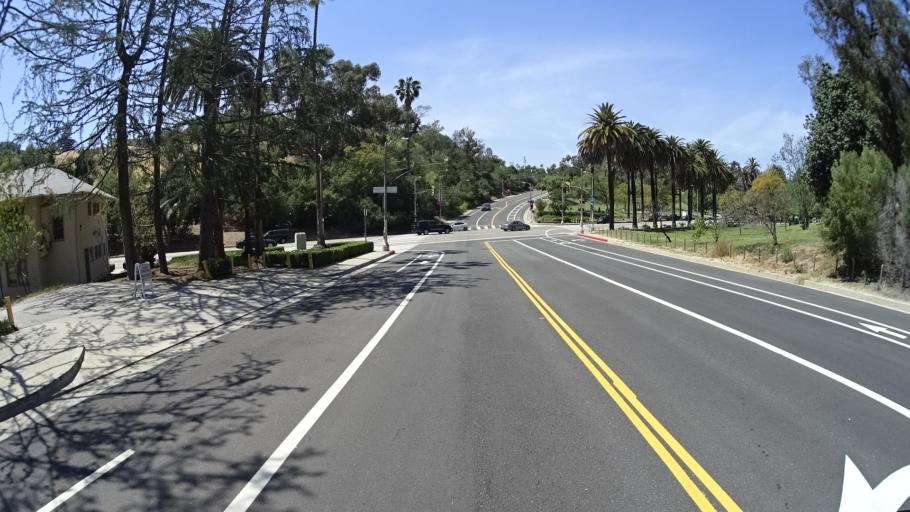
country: US
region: California
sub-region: Los Angeles County
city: Echo Park
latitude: 34.0770
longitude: -118.2483
